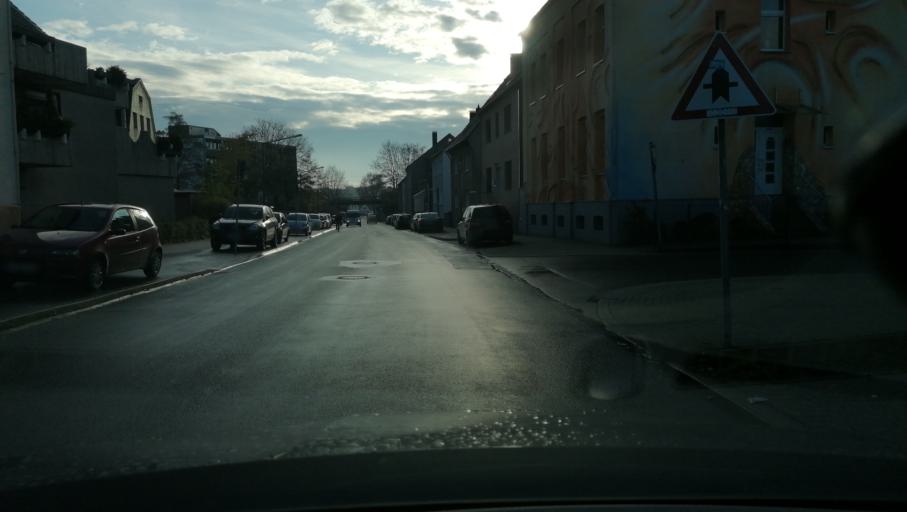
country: DE
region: North Rhine-Westphalia
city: Herten
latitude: 51.6009
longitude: 7.1538
